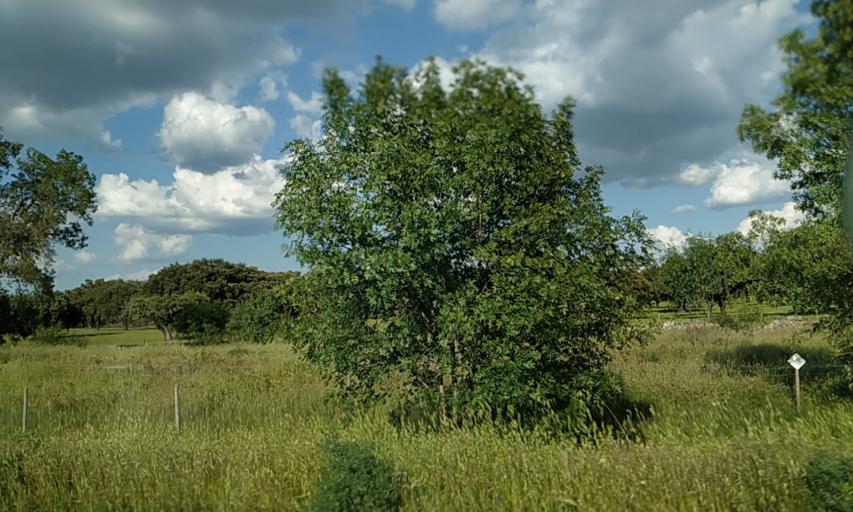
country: PT
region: Portalegre
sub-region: Portalegre
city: Urra
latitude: 39.2098
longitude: -7.4585
